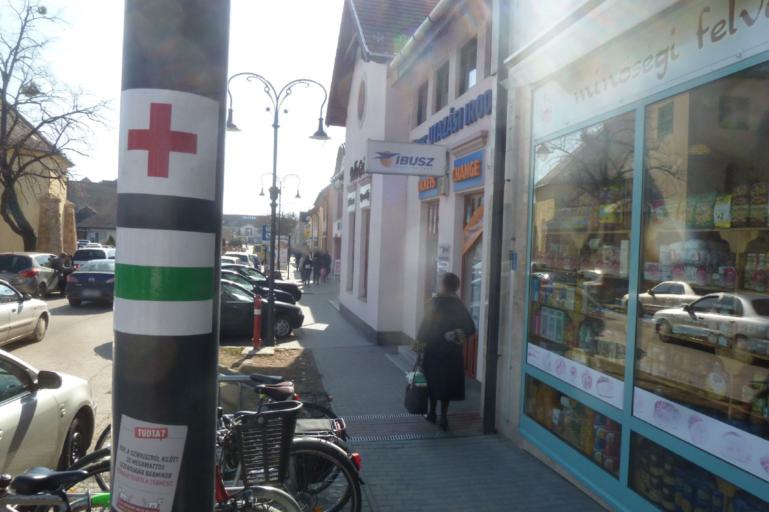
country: HU
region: Pest
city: Godollo
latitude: 47.6012
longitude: 19.3479
